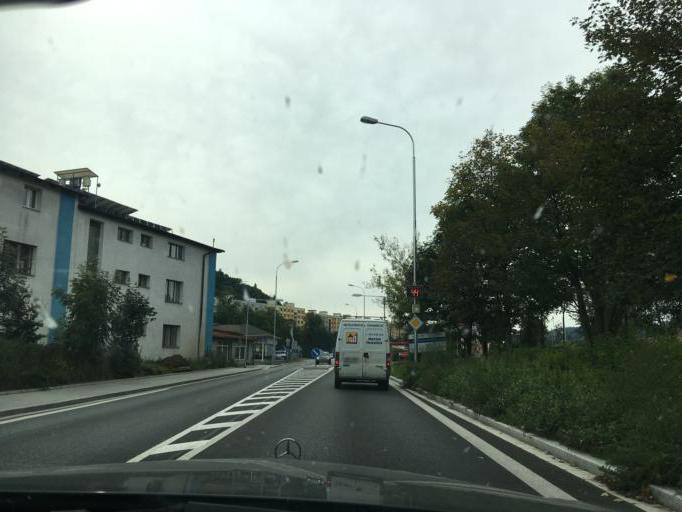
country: CZ
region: Kralovehradecky
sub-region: Okres Nachod
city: Nachod
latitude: 50.4191
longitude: 16.1795
